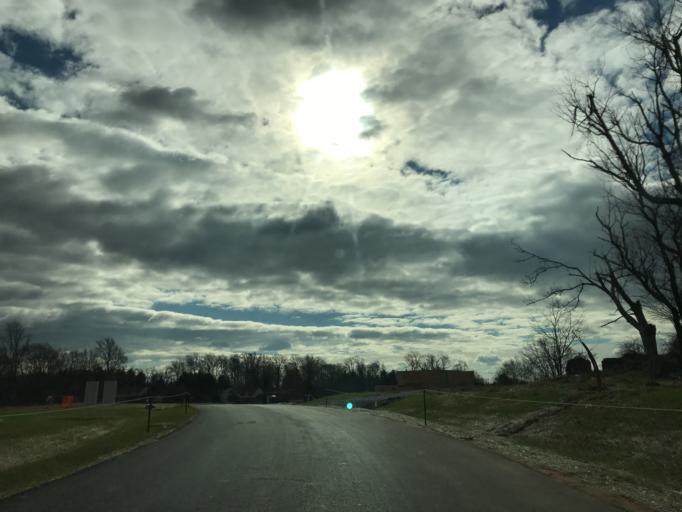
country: US
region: Maryland
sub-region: Harford County
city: Jarrettsville
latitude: 39.5141
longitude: -76.5295
